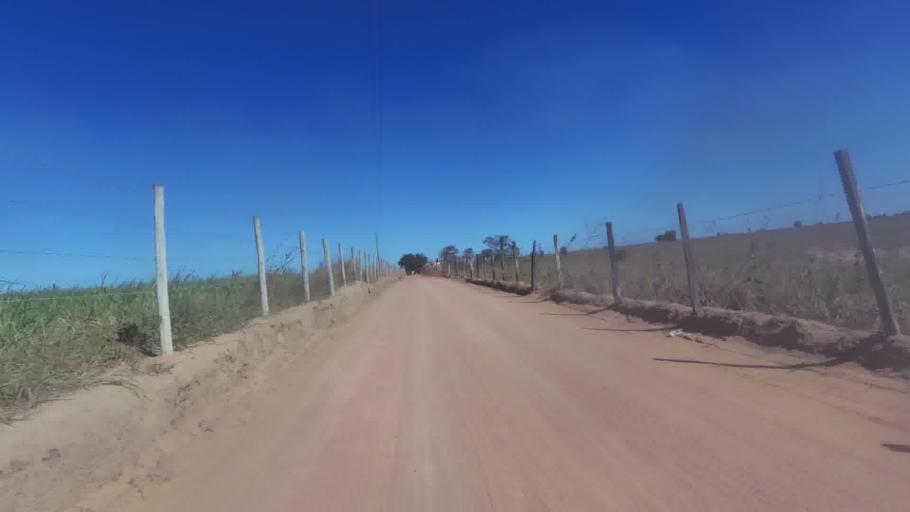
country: BR
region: Espirito Santo
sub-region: Marataizes
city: Marataizes
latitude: -21.1536
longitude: -40.9723
